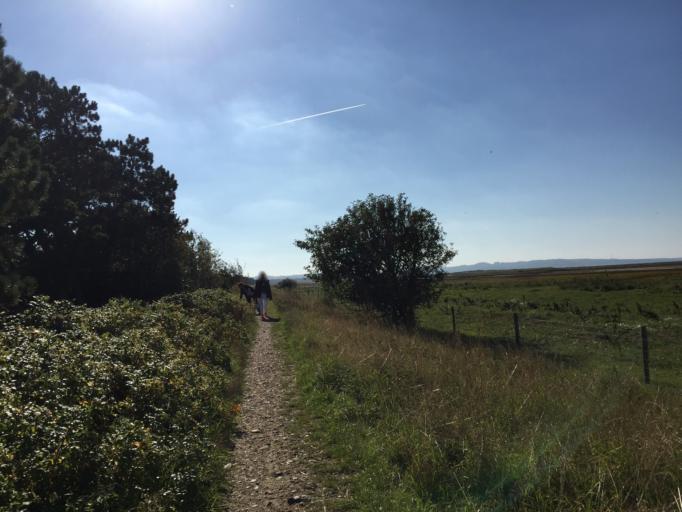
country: DK
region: Zealand
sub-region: Odsherred Kommune
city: Hojby
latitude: 55.8890
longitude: 11.5338
